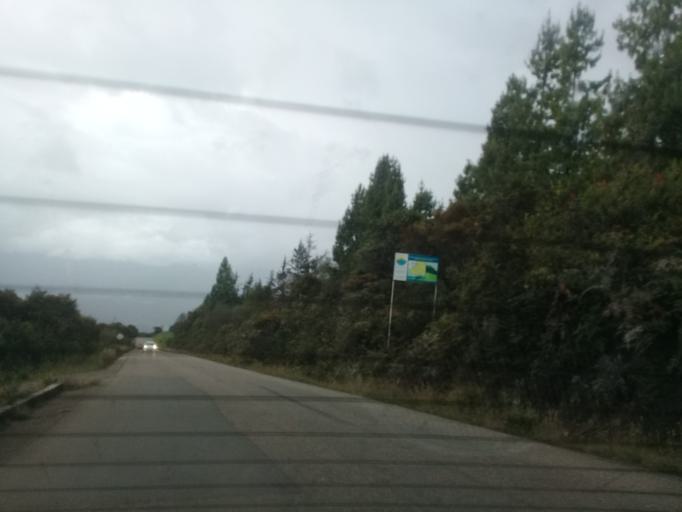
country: CO
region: Cundinamarca
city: Junin
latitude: 4.8452
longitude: -73.7452
